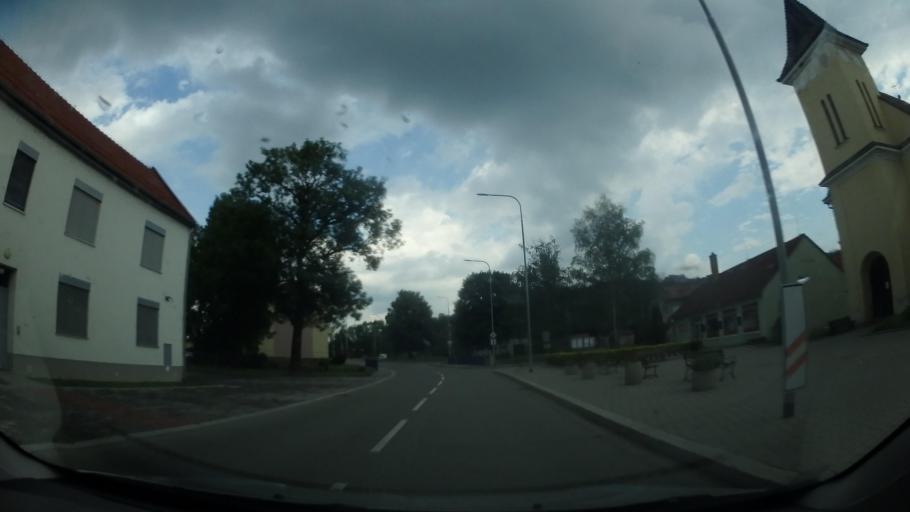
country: CZ
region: South Moravian
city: Svitavka
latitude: 49.4805
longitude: 16.6068
